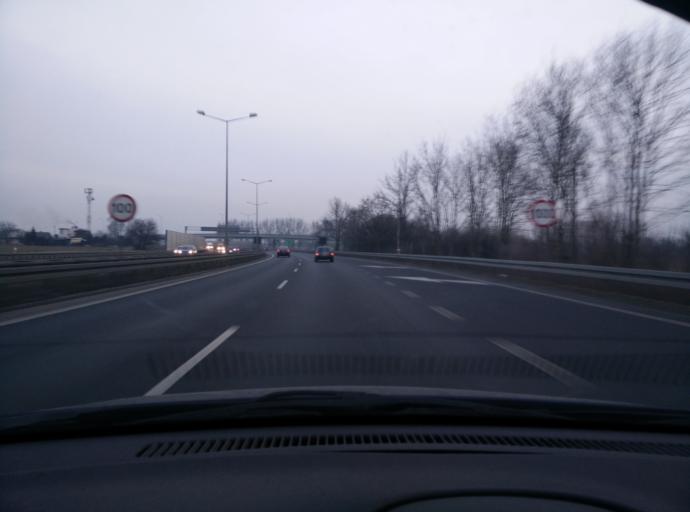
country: PL
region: Greater Poland Voivodeship
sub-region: Powiat poznanski
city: Daszewice
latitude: 52.3421
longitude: 17.0004
